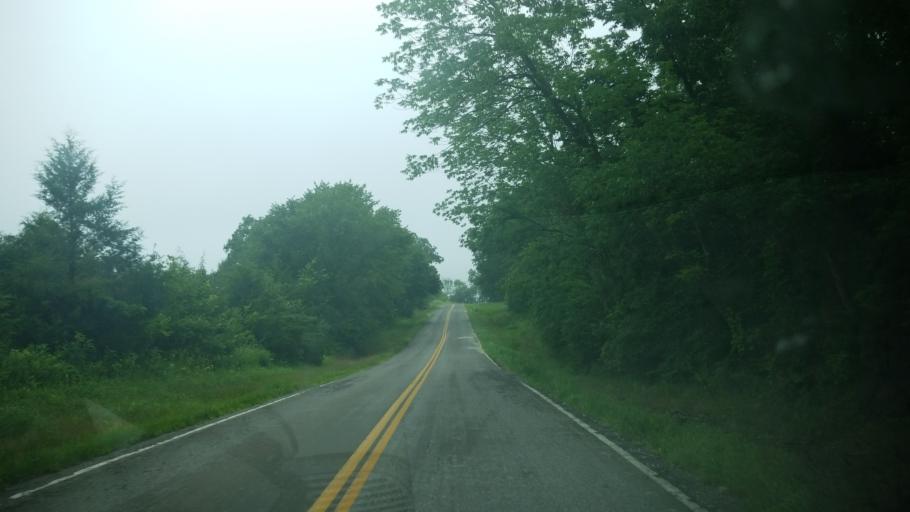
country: US
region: Missouri
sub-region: Audrain County
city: Vandalia
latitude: 39.2992
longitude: -91.3509
